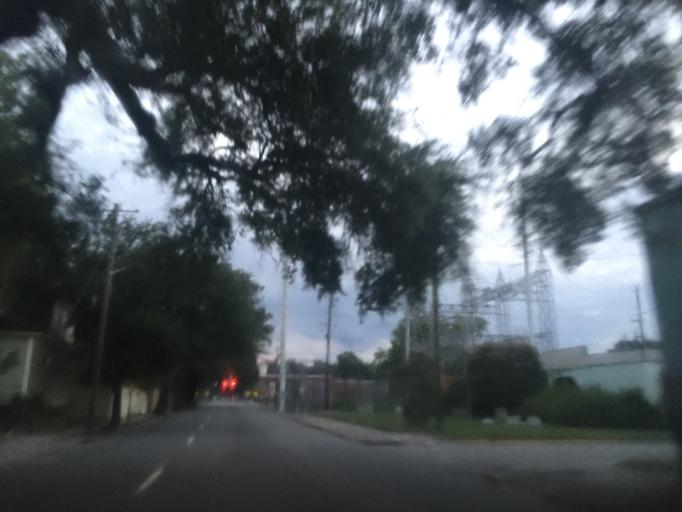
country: US
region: Georgia
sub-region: Chatham County
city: Savannah
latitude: 32.0636
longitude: -81.0898
